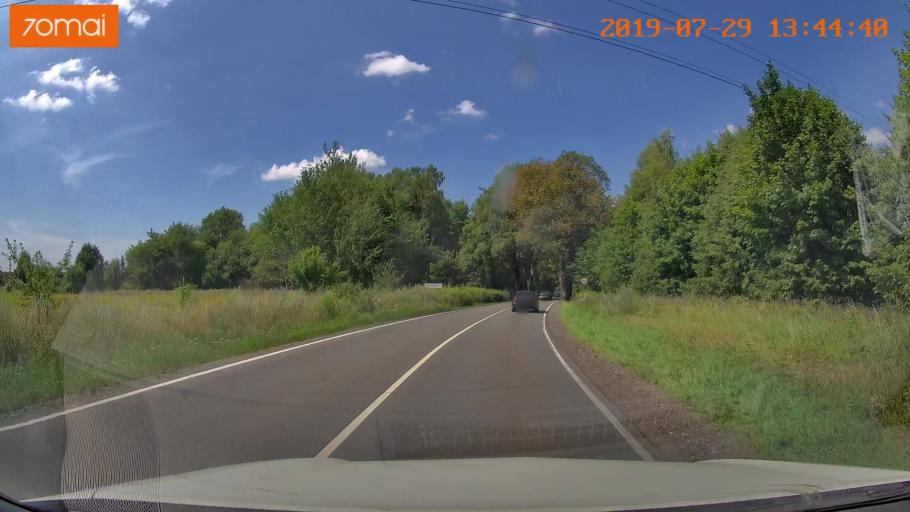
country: RU
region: Kaliningrad
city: Primorsk
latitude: 54.7381
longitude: 20.0849
